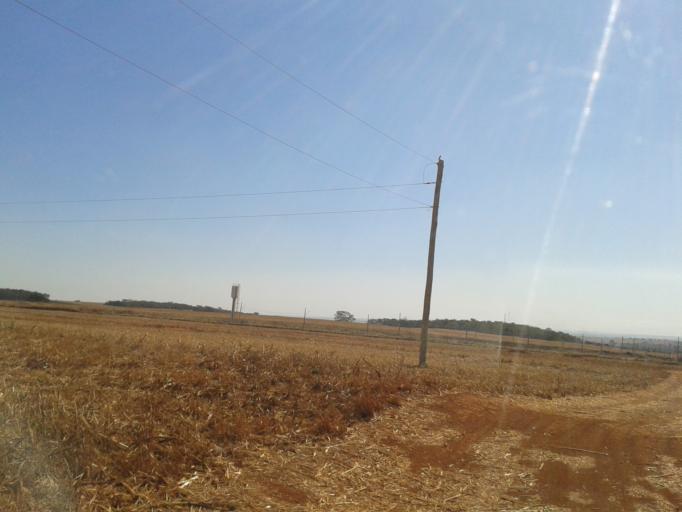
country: BR
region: Minas Gerais
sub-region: Capinopolis
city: Capinopolis
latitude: -18.6976
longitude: -49.5744
